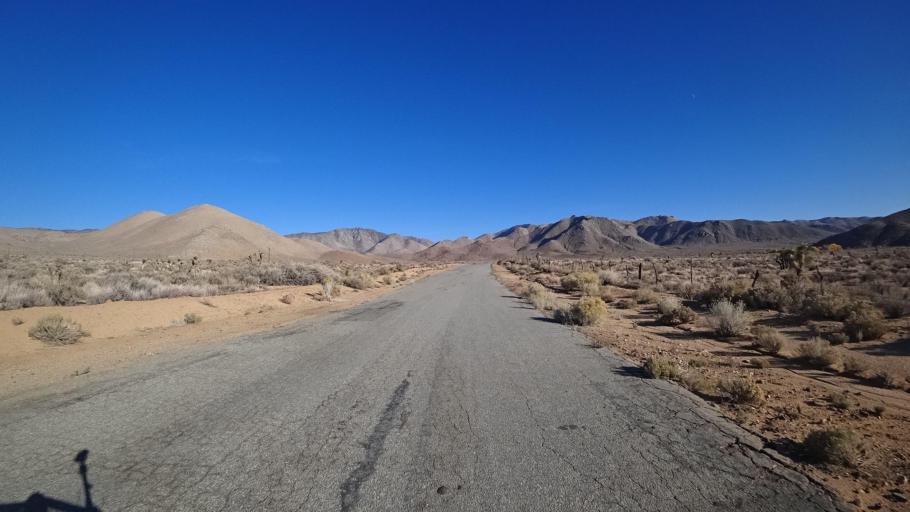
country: US
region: California
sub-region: Kern County
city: Weldon
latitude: 35.5553
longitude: -118.2182
